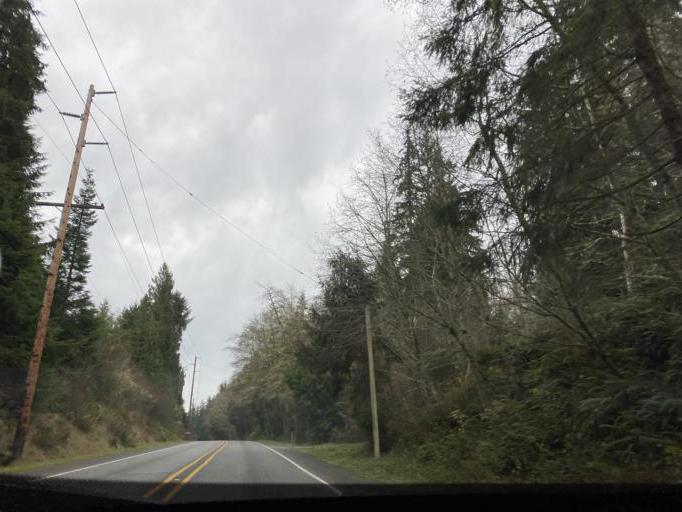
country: US
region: Washington
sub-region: Island County
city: Freeland
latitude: 48.0499
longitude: -122.5891
